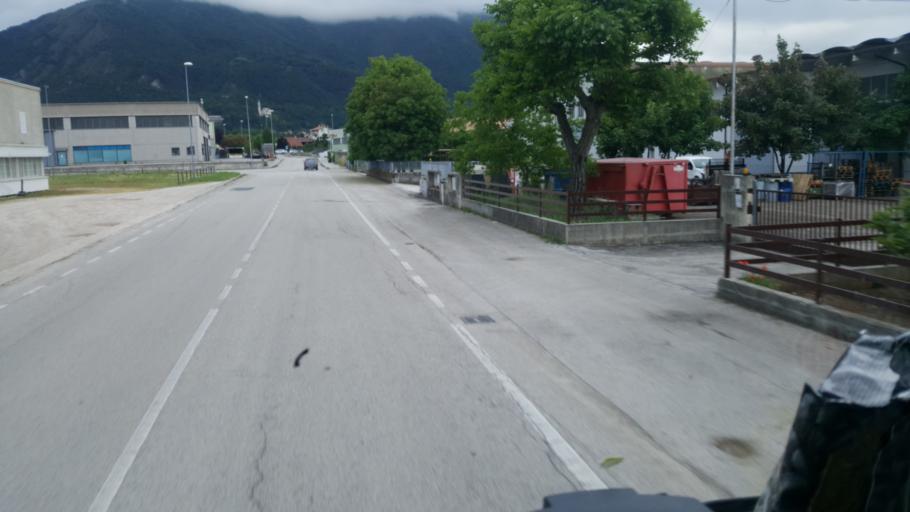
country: IT
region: Veneto
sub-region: Provincia di Vicenza
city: Santorso
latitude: 45.7220
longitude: 11.3933
